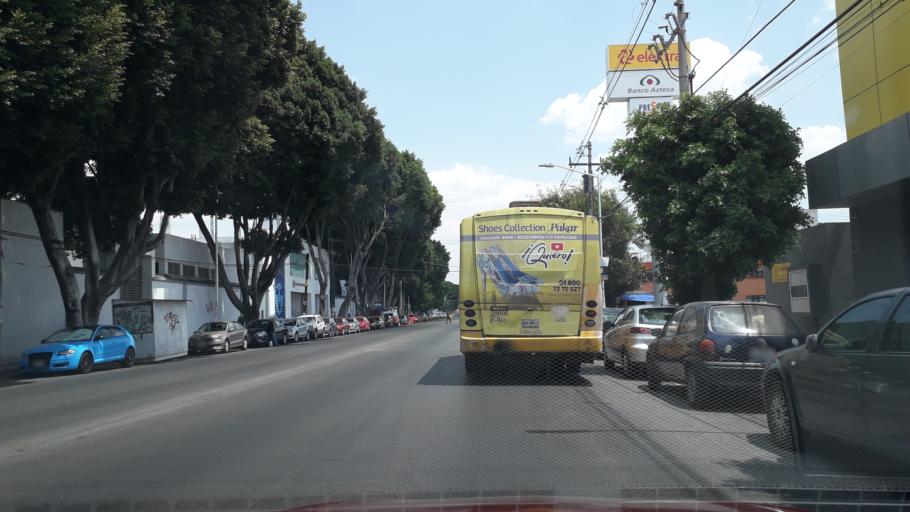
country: MX
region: Puebla
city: Puebla
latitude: 19.0382
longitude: -98.2163
